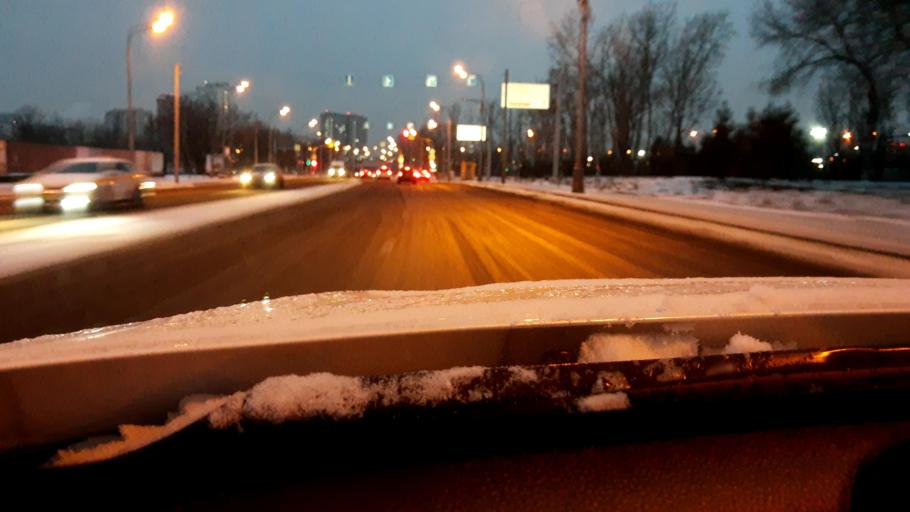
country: RU
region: Moskovskaya
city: Kozhukhovo
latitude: 55.7002
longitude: 37.6933
